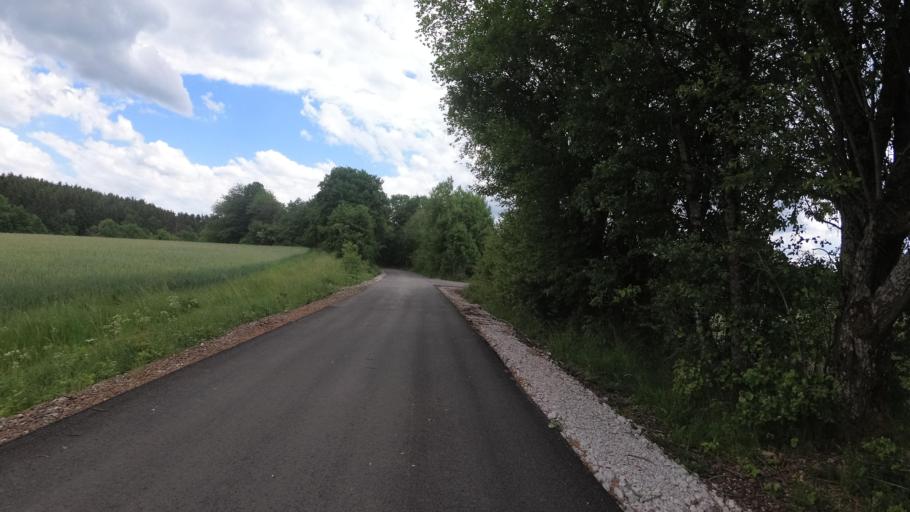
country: DE
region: Rheinland-Pfalz
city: Neuhutten
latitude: 49.6027
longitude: 7.0146
